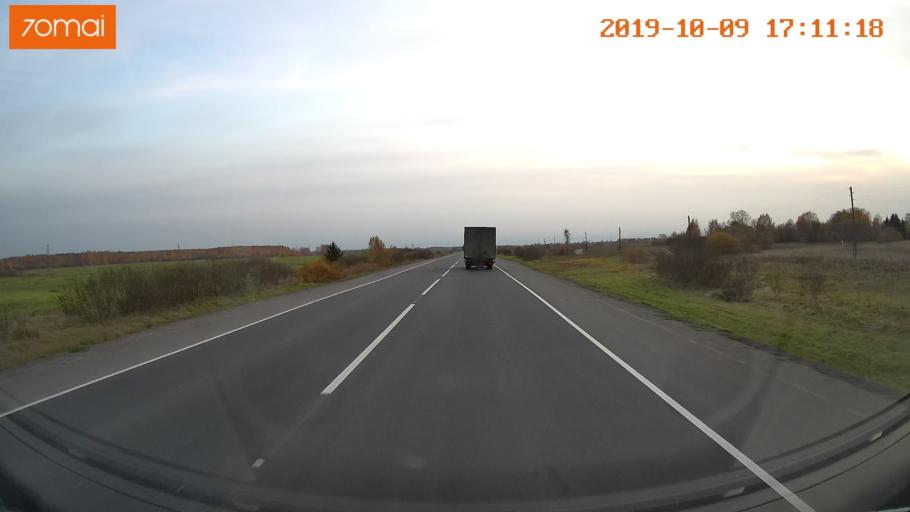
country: RU
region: Ivanovo
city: Privolzhsk
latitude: 57.3447
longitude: 41.2511
